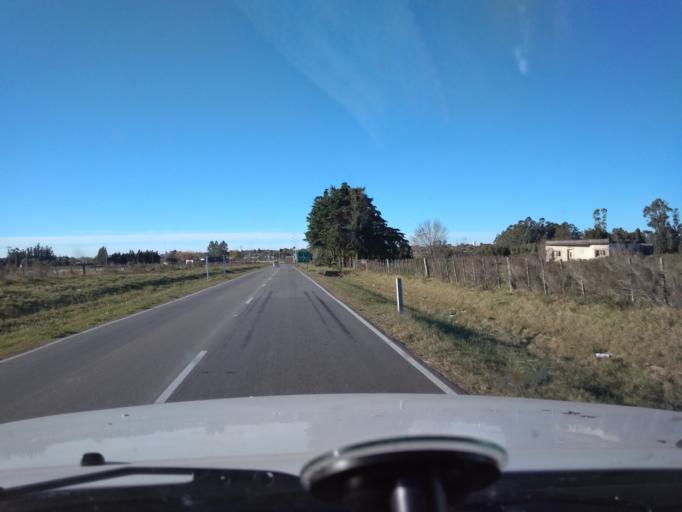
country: UY
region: Canelones
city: Santa Rosa
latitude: -34.5079
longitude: -56.0516
